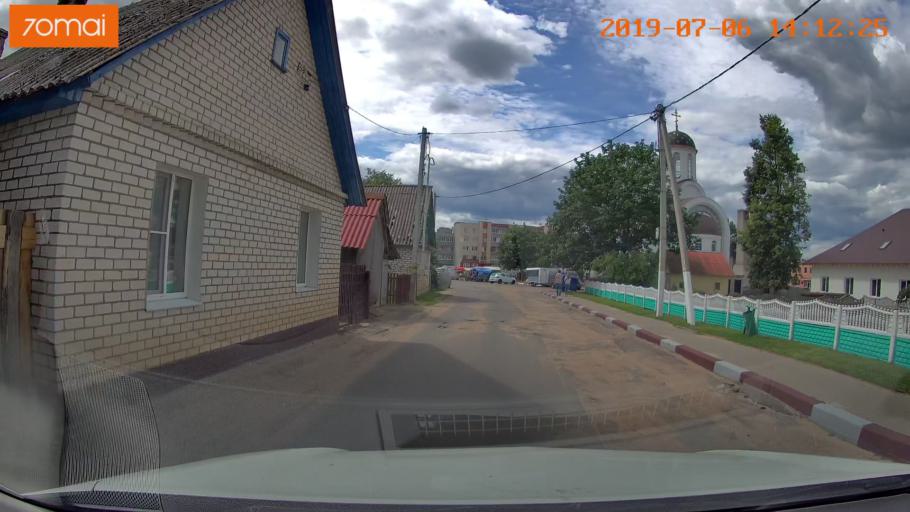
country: BY
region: Minsk
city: Ivyanyets
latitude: 53.8894
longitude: 26.7428
